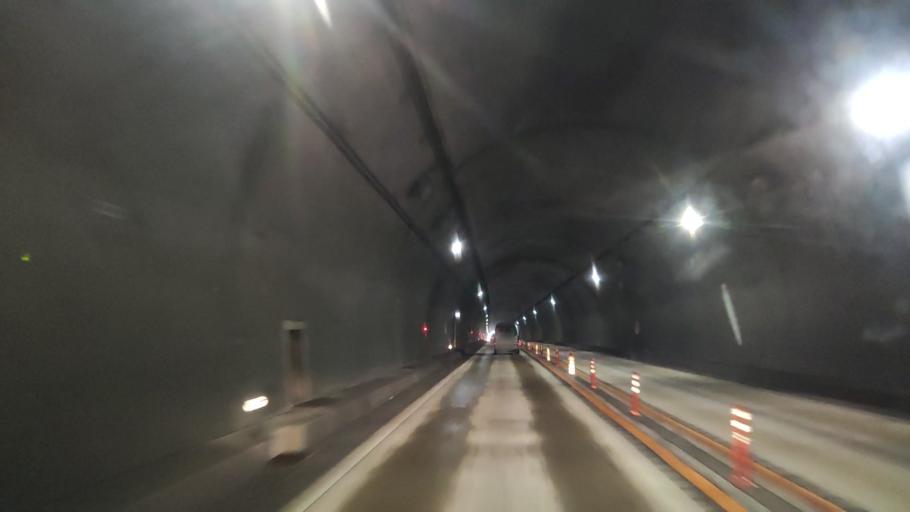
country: JP
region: Tokushima
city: Kamojimacho-jogejima
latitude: 34.1127
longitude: 134.3213
